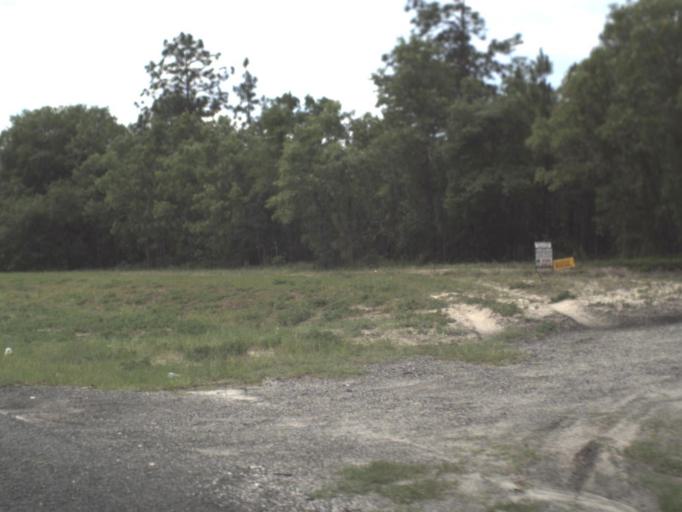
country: US
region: Florida
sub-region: Nassau County
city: Hilliard
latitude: 30.7517
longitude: -81.9602
